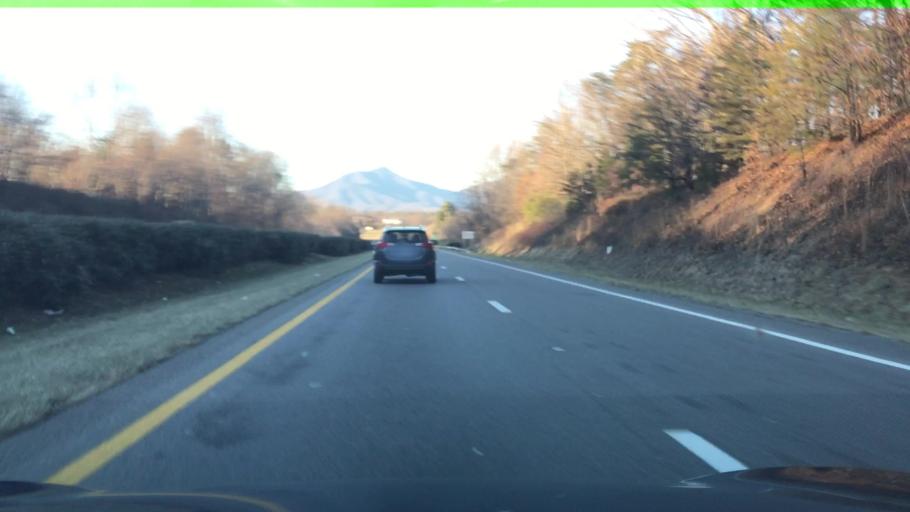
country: US
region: Virginia
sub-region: City of Bedford
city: Bedford
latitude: 37.3295
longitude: -79.5411
